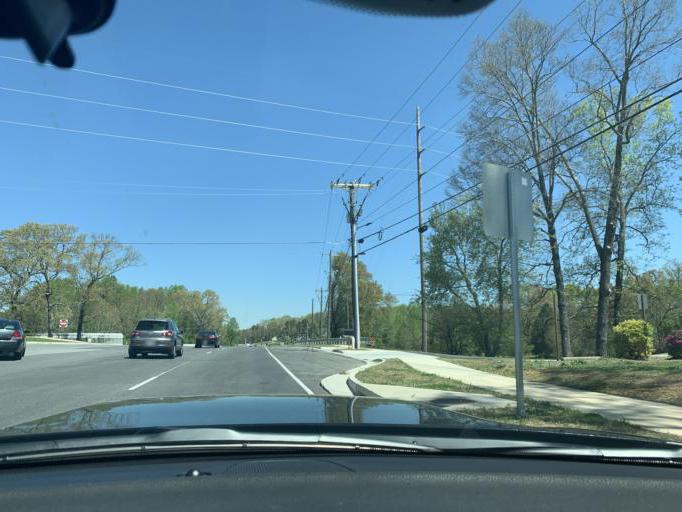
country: US
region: Georgia
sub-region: Forsyth County
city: Cumming
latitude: 34.1966
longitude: -84.1971
